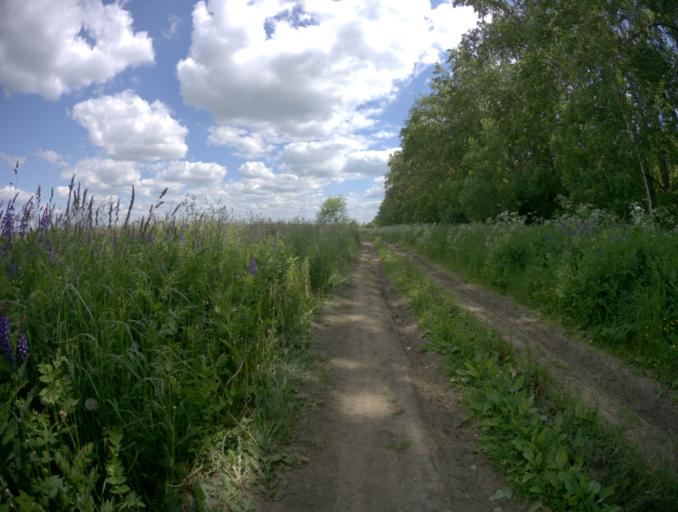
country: RU
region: Vladimir
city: Bogolyubovo
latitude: 56.1824
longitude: 40.4798
